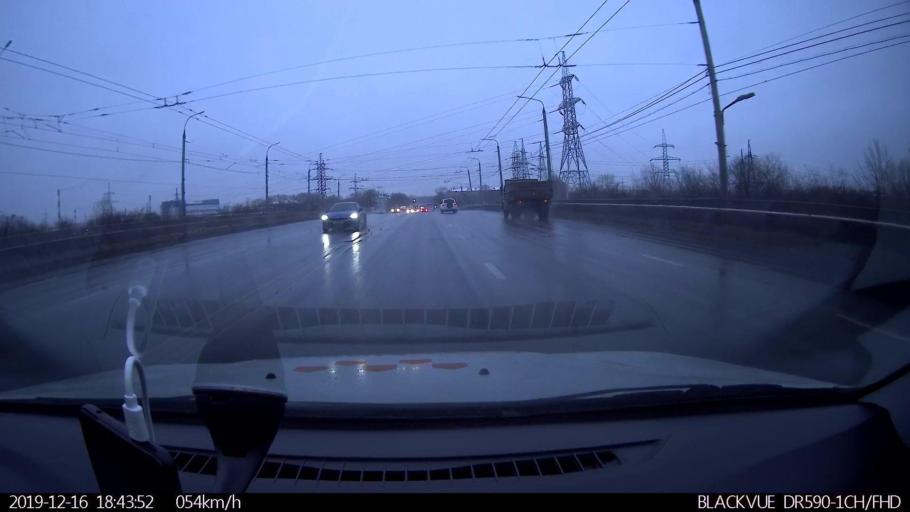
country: RU
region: Nizjnij Novgorod
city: Nizhniy Novgorod
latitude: 56.2600
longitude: 43.9082
